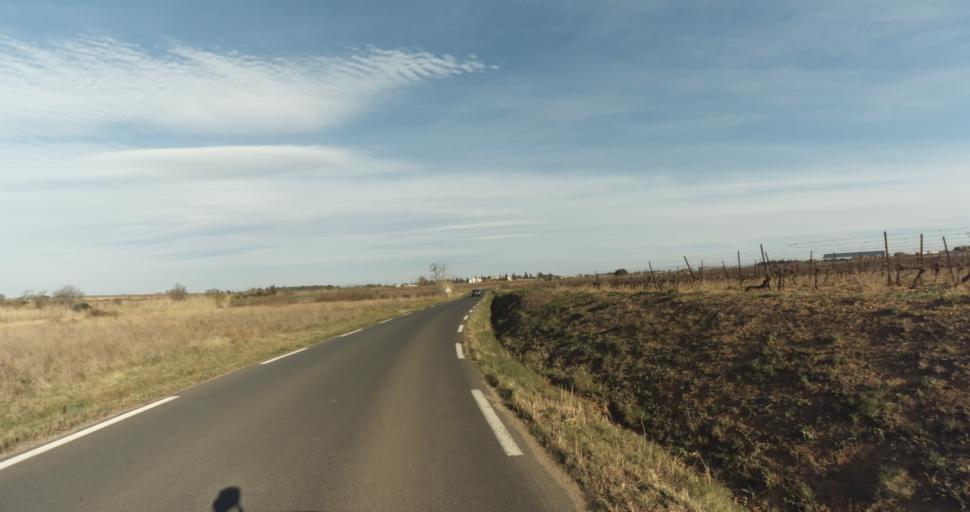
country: FR
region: Languedoc-Roussillon
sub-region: Departement de l'Herault
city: Pomerols
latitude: 43.3782
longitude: 3.5115
